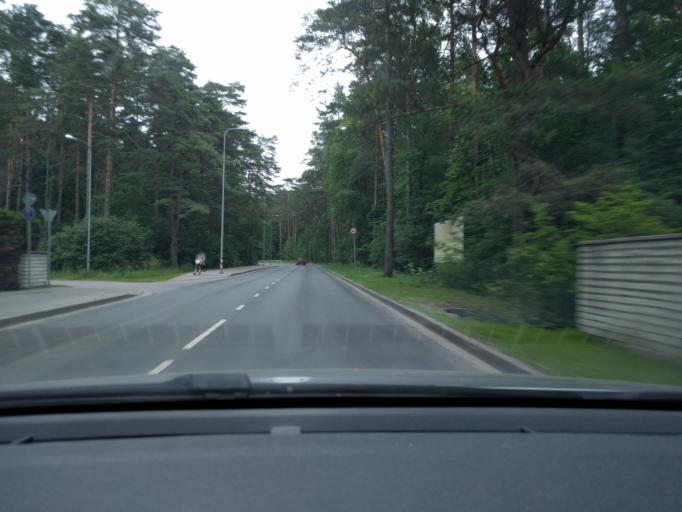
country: EE
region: Harju
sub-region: Viimsi vald
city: Viimsi
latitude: 59.4747
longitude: 24.8432
